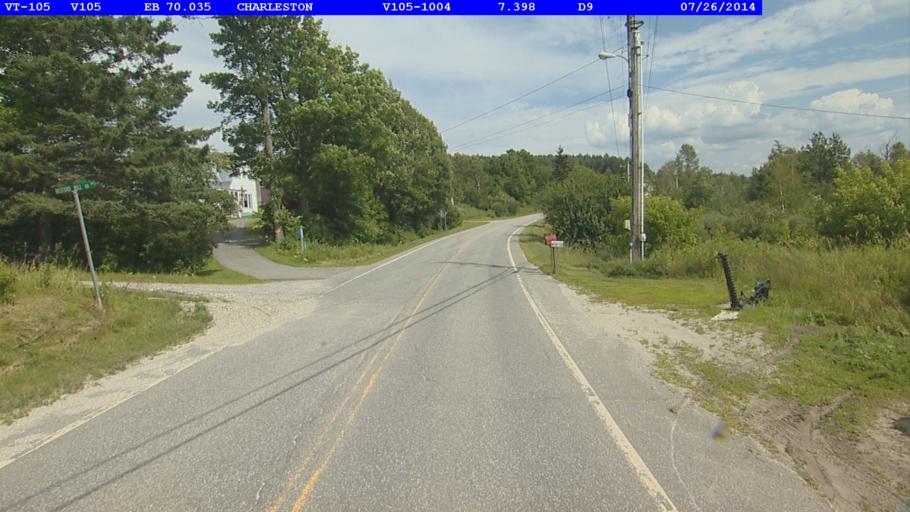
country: US
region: Vermont
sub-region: Orleans County
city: Newport
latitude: 44.8365
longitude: -71.9839
